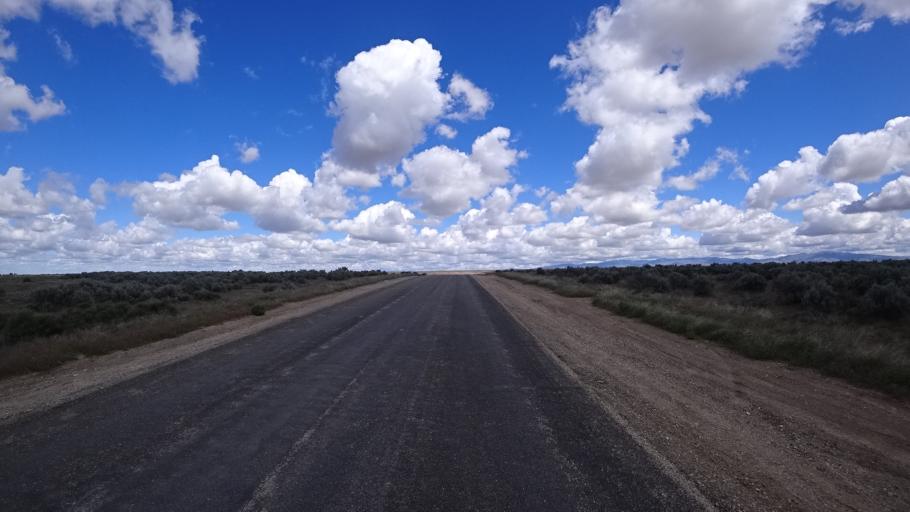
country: US
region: Idaho
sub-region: Ada County
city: Garden City
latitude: 43.4814
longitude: -116.2743
